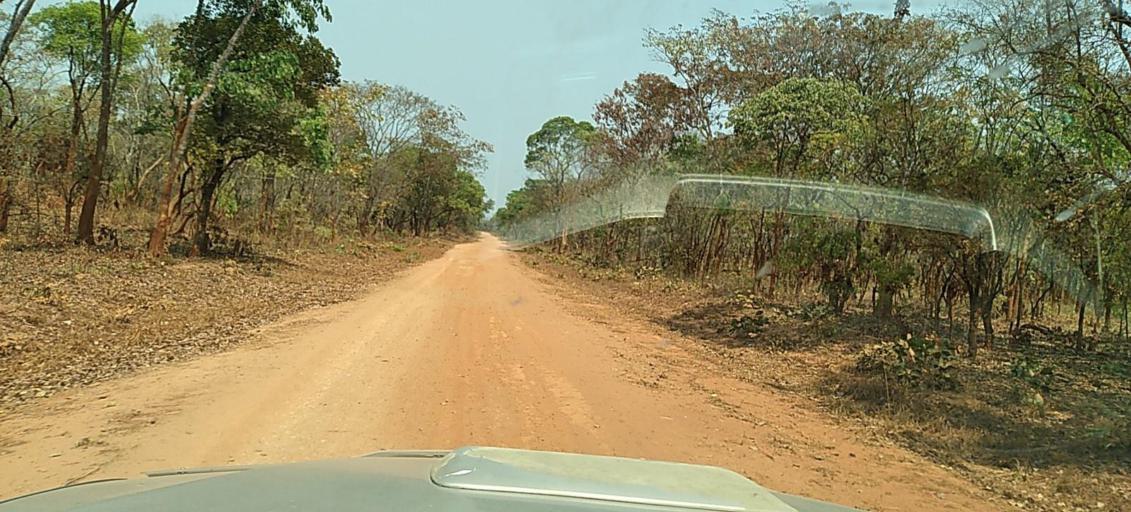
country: ZM
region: North-Western
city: Kasempa
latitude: -13.6861
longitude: 26.3200
